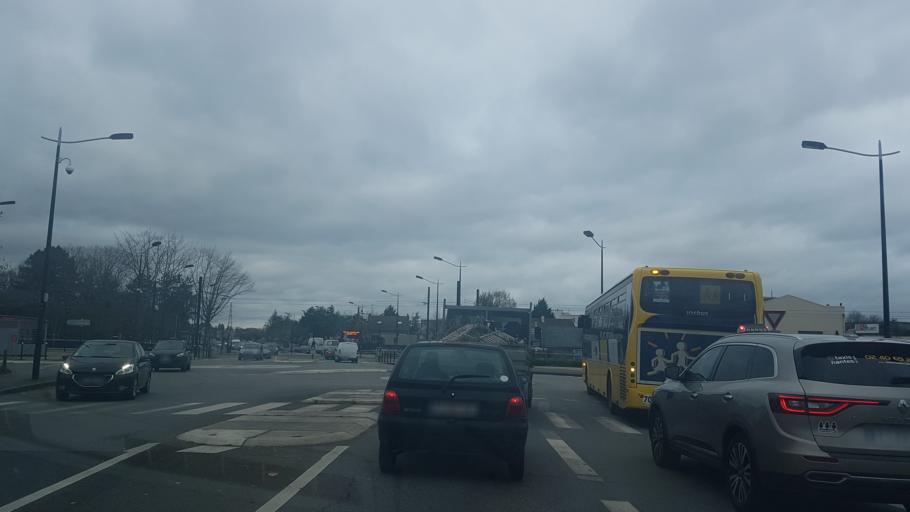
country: FR
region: Pays de la Loire
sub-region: Departement de la Loire-Atlantique
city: Nantes
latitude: 47.2524
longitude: -1.5299
